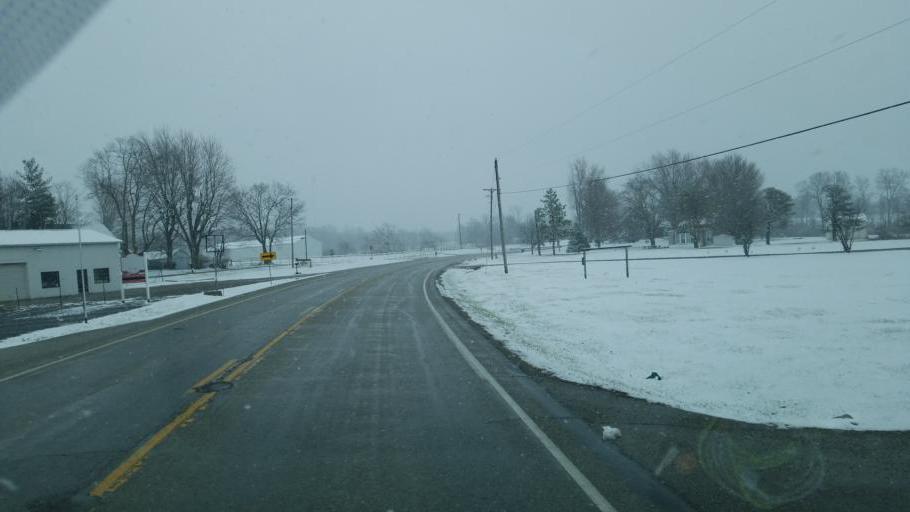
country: US
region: Indiana
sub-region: Wayne County
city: Richmond
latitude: 39.8997
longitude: -84.9457
